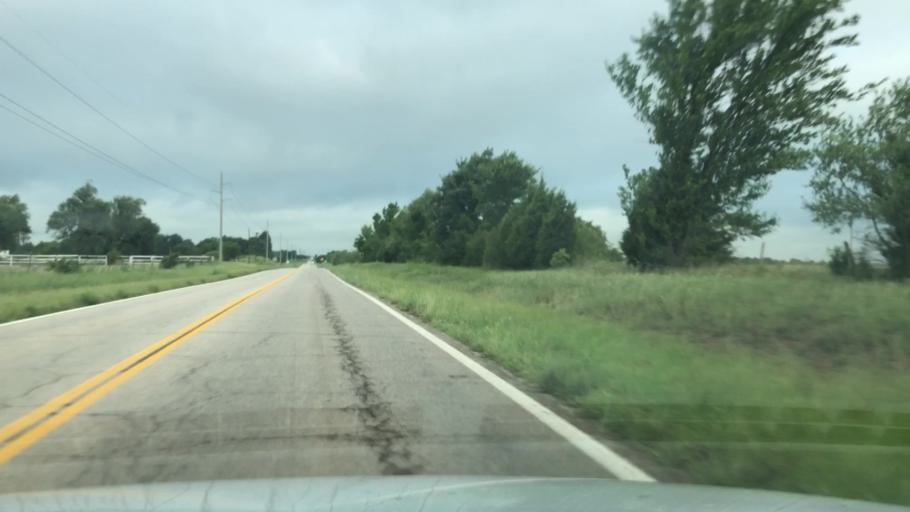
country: US
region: Oklahoma
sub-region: Nowata County
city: Nowata
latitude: 36.7136
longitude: -95.6729
